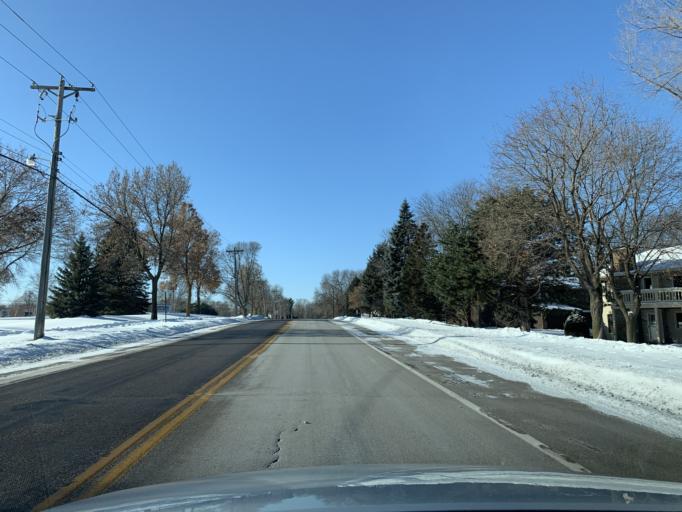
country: US
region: Minnesota
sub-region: Hennepin County
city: Edina
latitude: 44.8332
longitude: -93.3568
